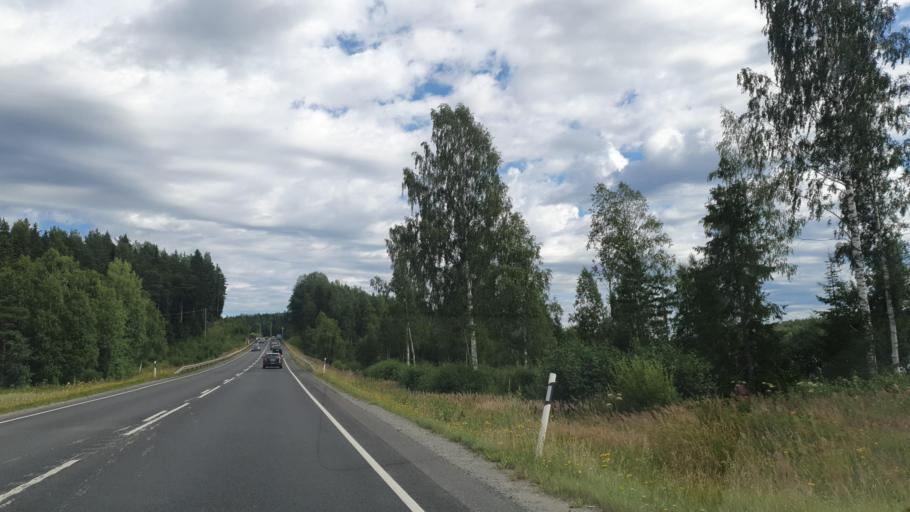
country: FI
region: Central Finland
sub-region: Jyvaeskylae
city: Korpilahti
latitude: 61.9920
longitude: 25.4550
